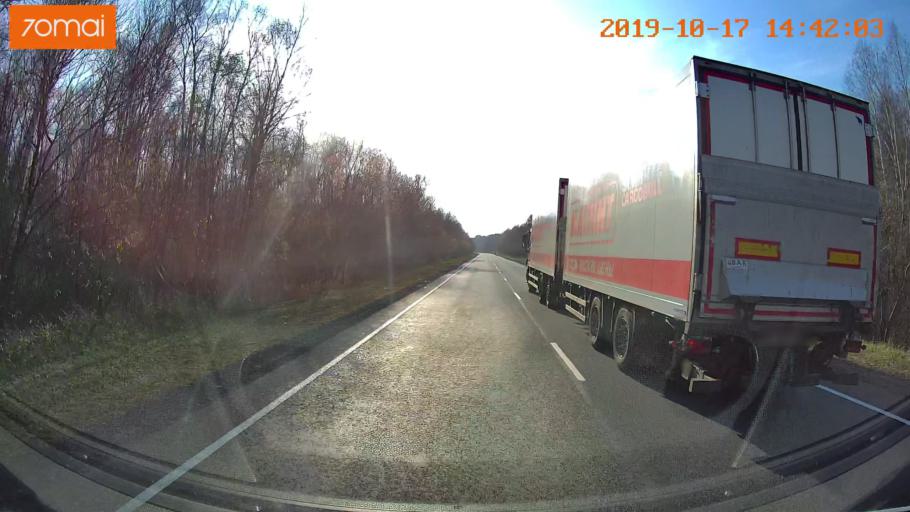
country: RU
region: Rjazan
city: Solotcha
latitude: 54.8406
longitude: 39.9316
